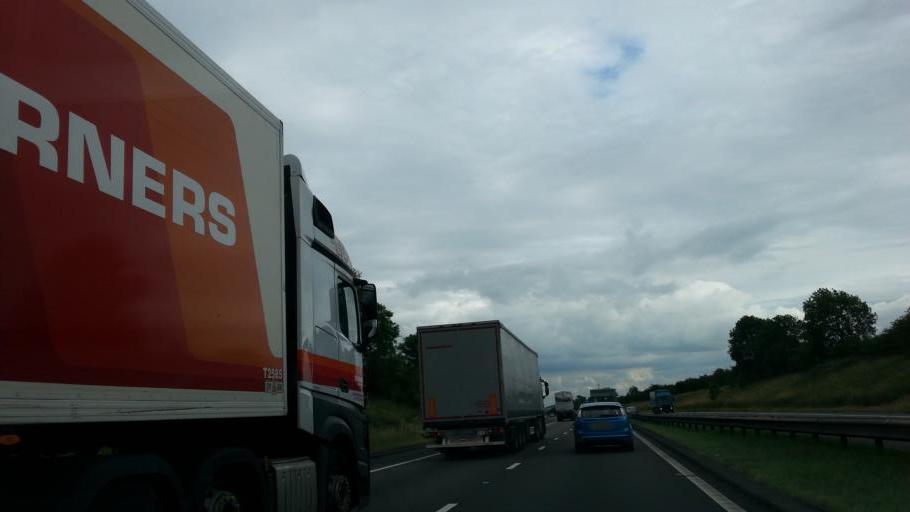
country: GB
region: England
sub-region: Doncaster
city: Tickhill
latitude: 53.4630
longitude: -1.1289
